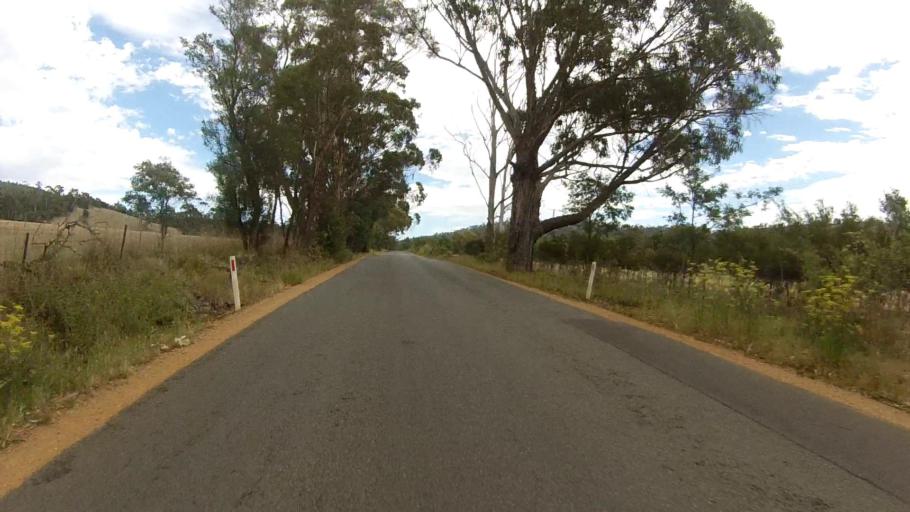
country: AU
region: Tasmania
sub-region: Clarence
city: Lindisfarne
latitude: -42.7506
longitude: 147.3750
